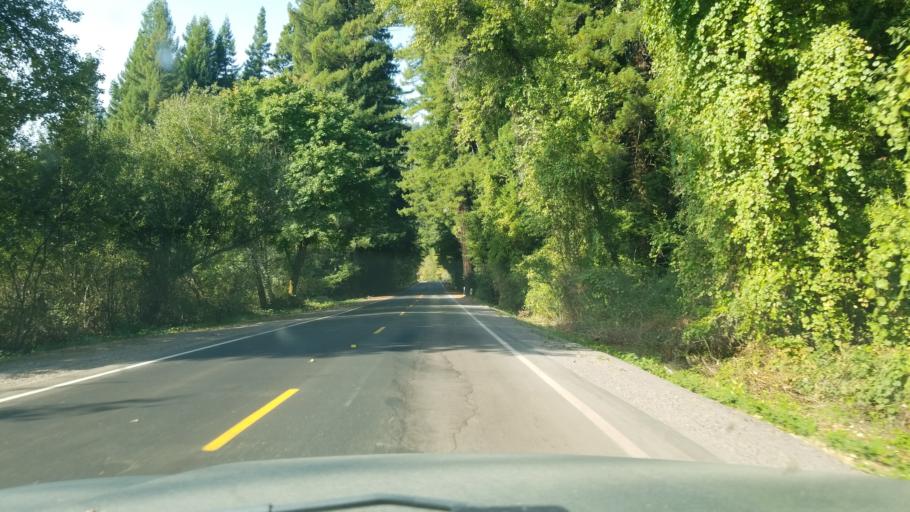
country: US
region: California
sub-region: Humboldt County
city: Redway
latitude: 40.2164
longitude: -123.7864
